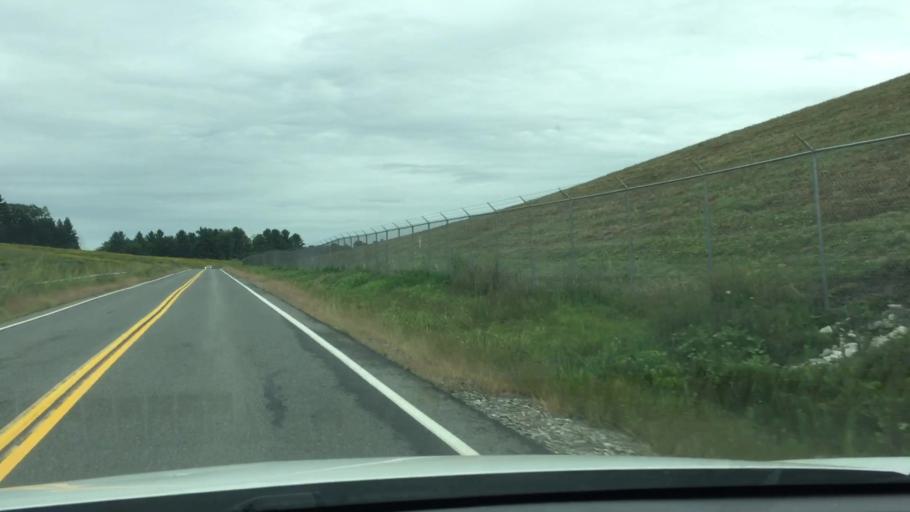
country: US
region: Massachusetts
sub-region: Berkshire County
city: Pittsfield
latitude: 42.4321
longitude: -73.2822
